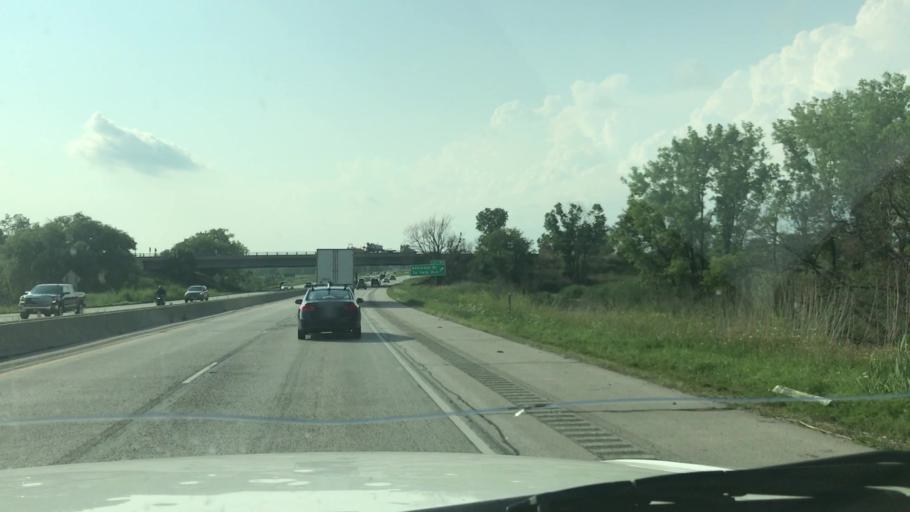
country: US
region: Wisconsin
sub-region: Brown County
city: Green Bay
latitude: 44.5392
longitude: -88.0230
